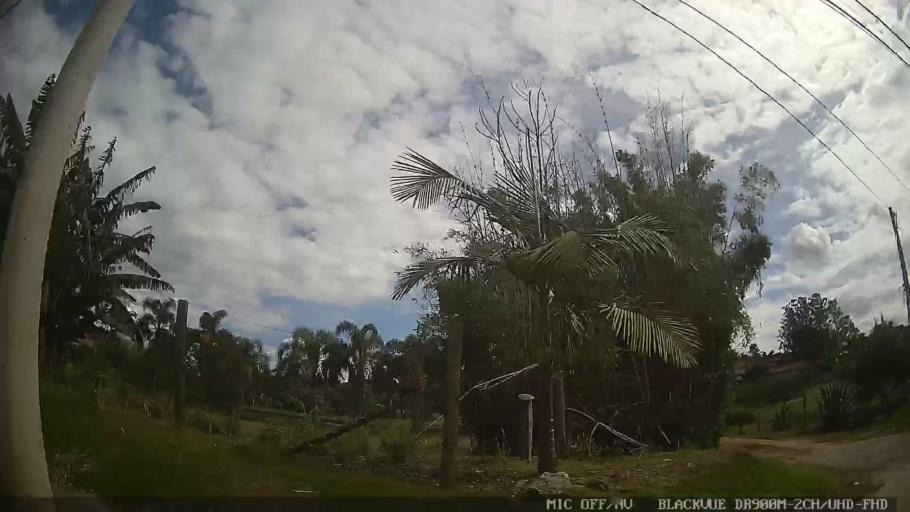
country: BR
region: Sao Paulo
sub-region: Mogi das Cruzes
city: Mogi das Cruzes
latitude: -23.5719
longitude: -46.2007
